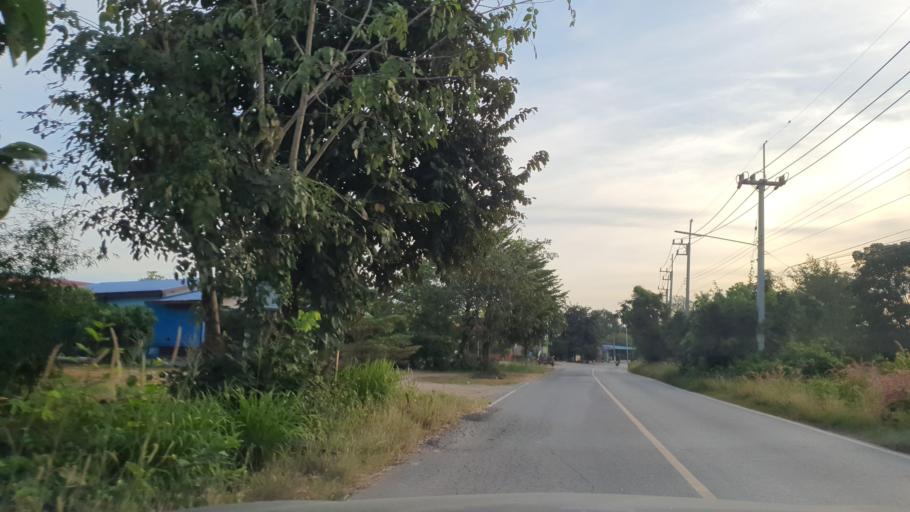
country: TH
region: Nakhon Sawan
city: Nakhon Sawan
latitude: 15.6632
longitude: 100.0556
